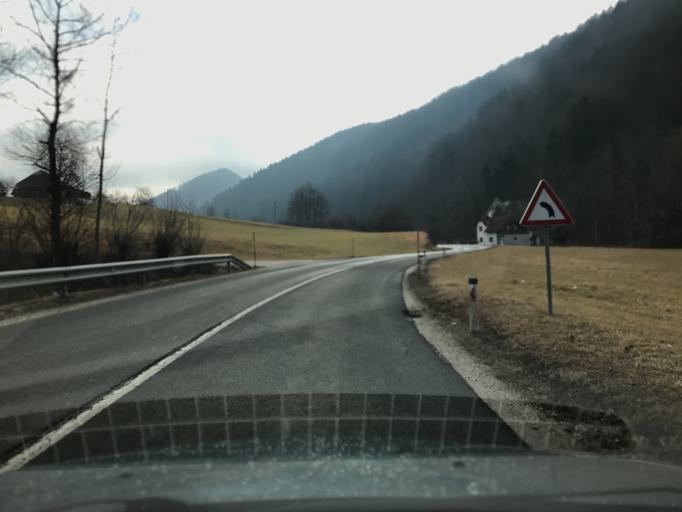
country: SI
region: Lukovica
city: Lukovica pri Domzalah
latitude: 46.2179
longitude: 14.7116
